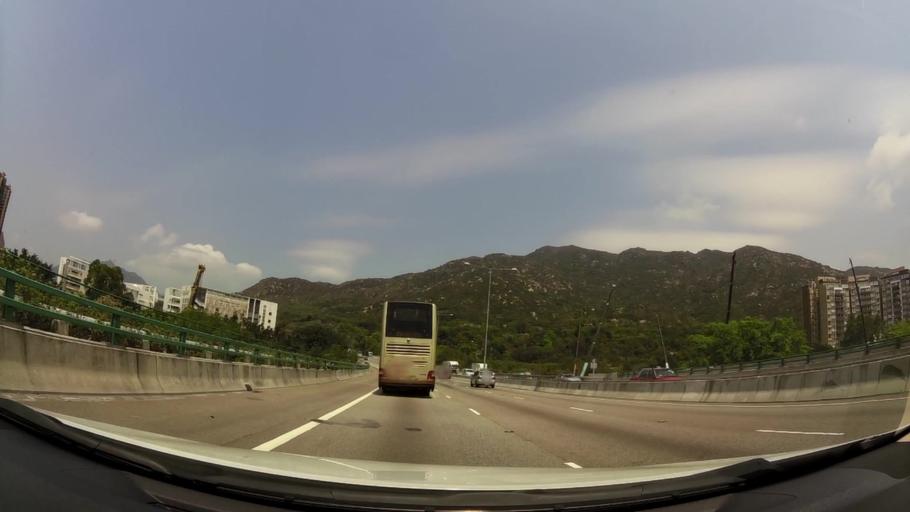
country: HK
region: Tuen Mun
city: Tuen Mun
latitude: 22.3732
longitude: 113.9978
